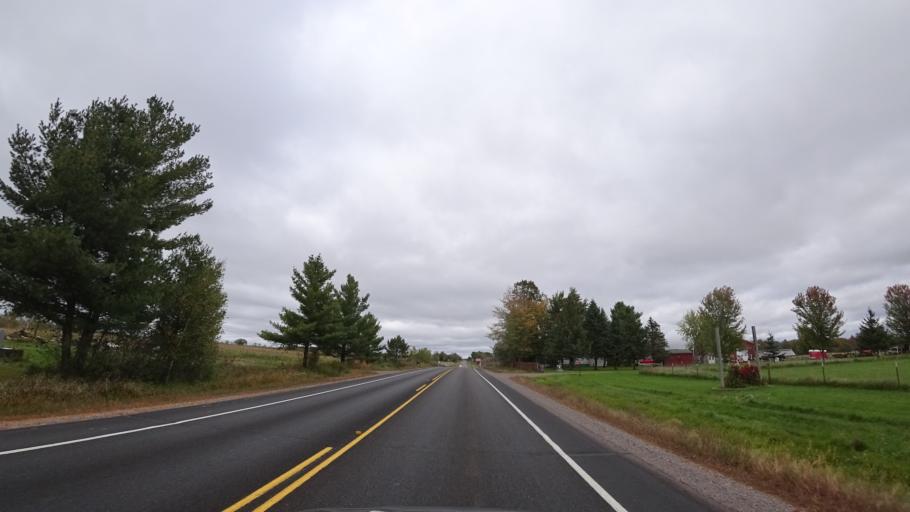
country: US
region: Wisconsin
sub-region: Rusk County
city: Ladysmith
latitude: 45.3623
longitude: -91.1107
